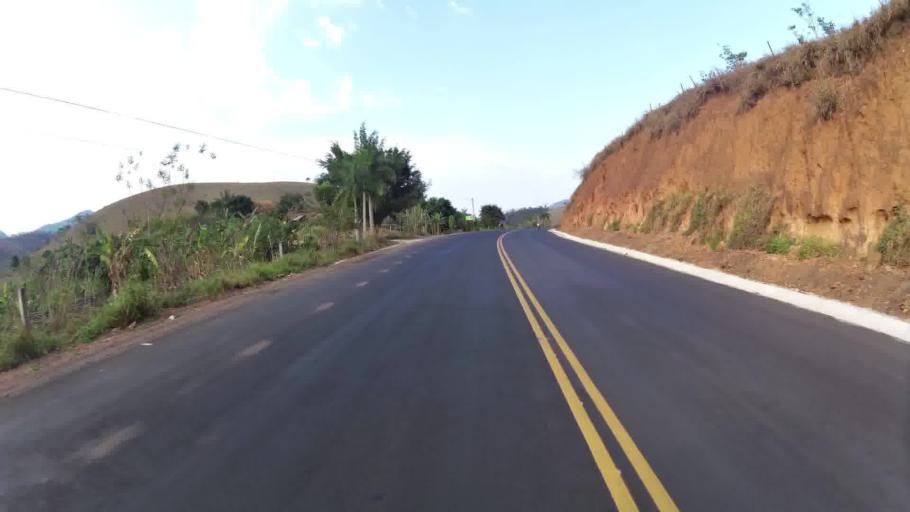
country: BR
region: Rio de Janeiro
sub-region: Santo Antonio De Padua
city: Santo Antonio de Padua
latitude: -21.4885
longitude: -42.0648
